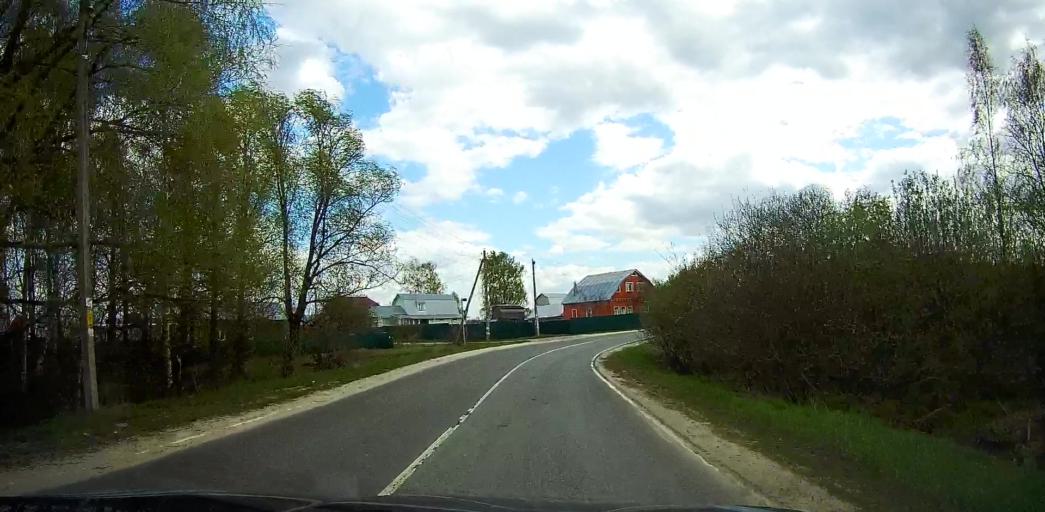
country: RU
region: Moskovskaya
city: Davydovo
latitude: 55.6457
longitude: 38.7505
